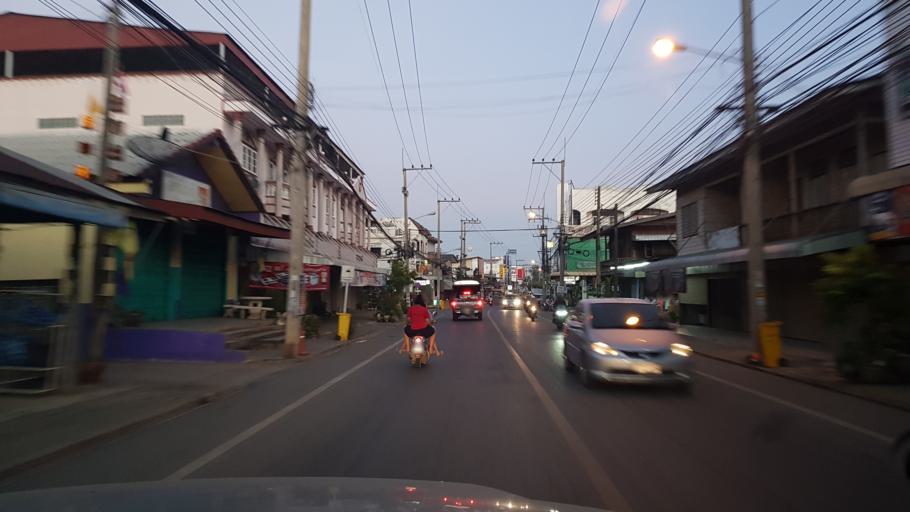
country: TH
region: Chaiyaphum
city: Phu Khiao
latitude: 16.3660
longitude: 102.1359
